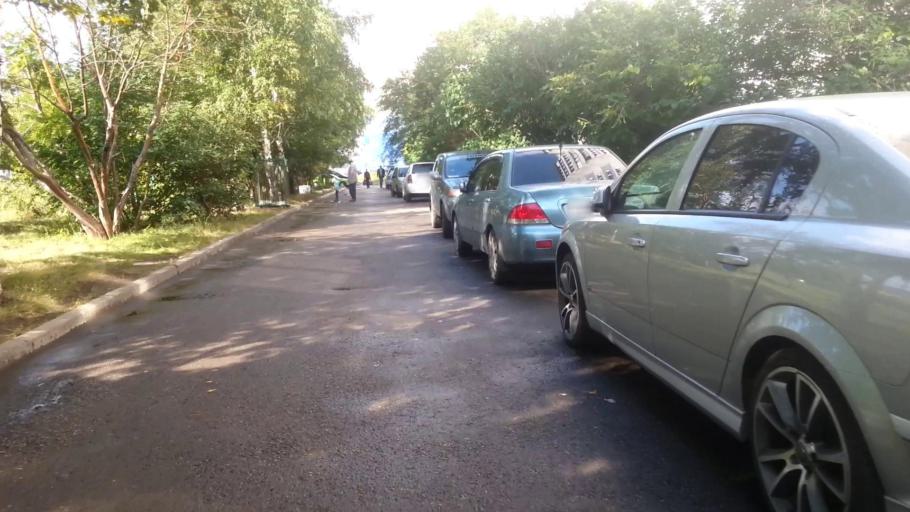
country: RU
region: Altai Krai
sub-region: Gorod Barnaulskiy
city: Barnaul
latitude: 53.3547
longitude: 83.6991
